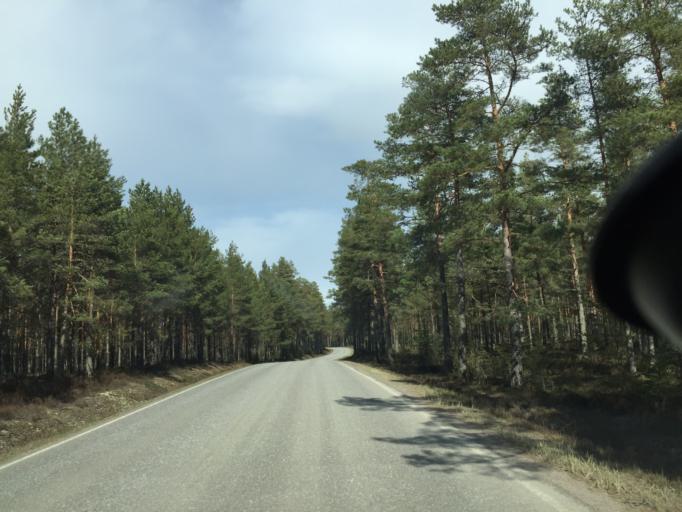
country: FI
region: Uusimaa
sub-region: Raaseporin
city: Hanko
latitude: 59.9584
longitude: 22.9673
